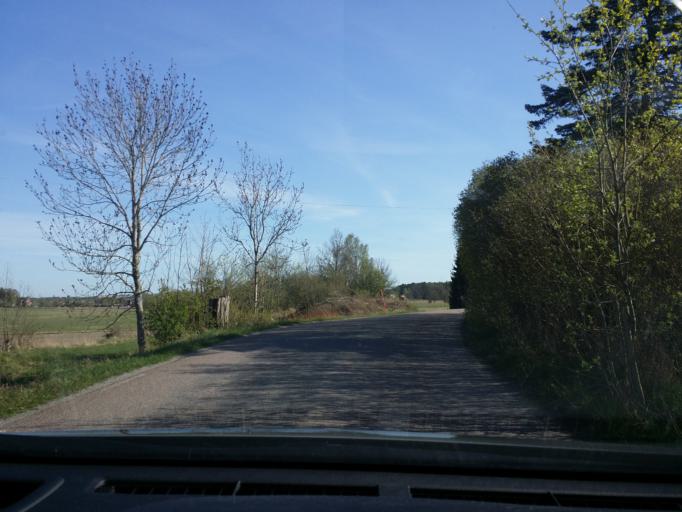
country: SE
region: Vaestmanland
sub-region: Vasteras
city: Vasteras
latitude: 59.6402
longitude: 16.4810
